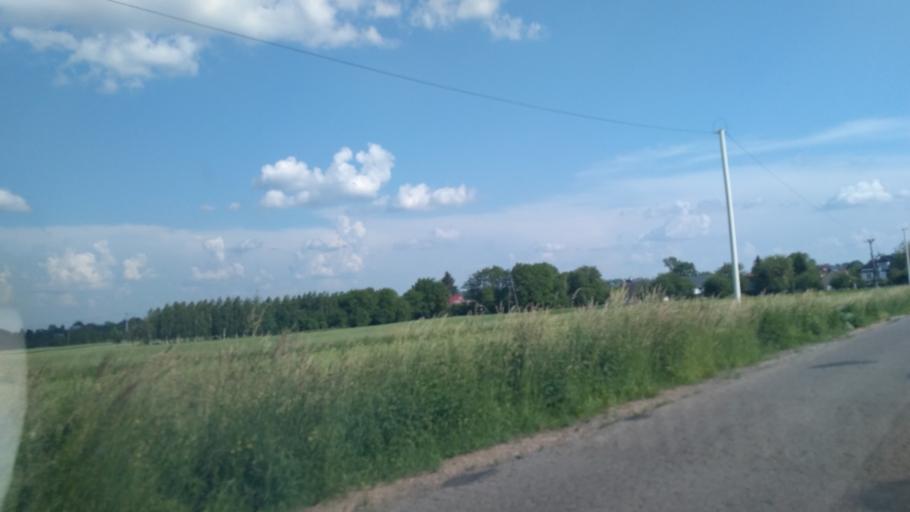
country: PL
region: Subcarpathian Voivodeship
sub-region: Powiat jaroslawski
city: Ostrow
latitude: 49.9314
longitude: 22.7406
